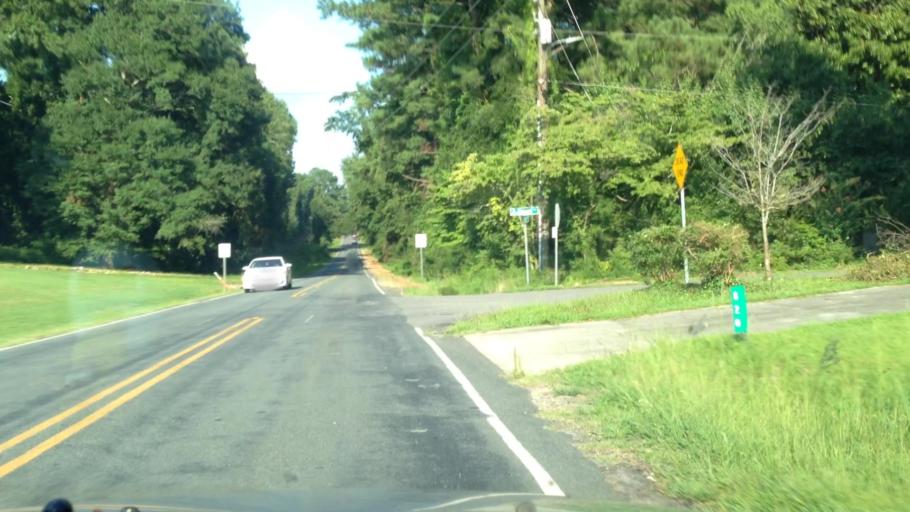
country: US
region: North Carolina
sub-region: Harnett County
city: Buies Creek
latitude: 35.4084
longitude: -78.7329
